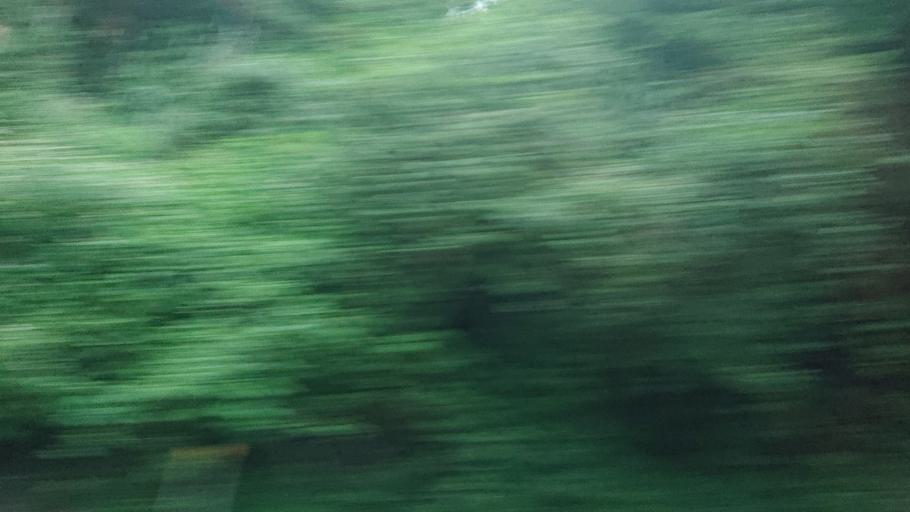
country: TW
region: Taiwan
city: Lugu
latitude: 23.5074
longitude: 120.6963
